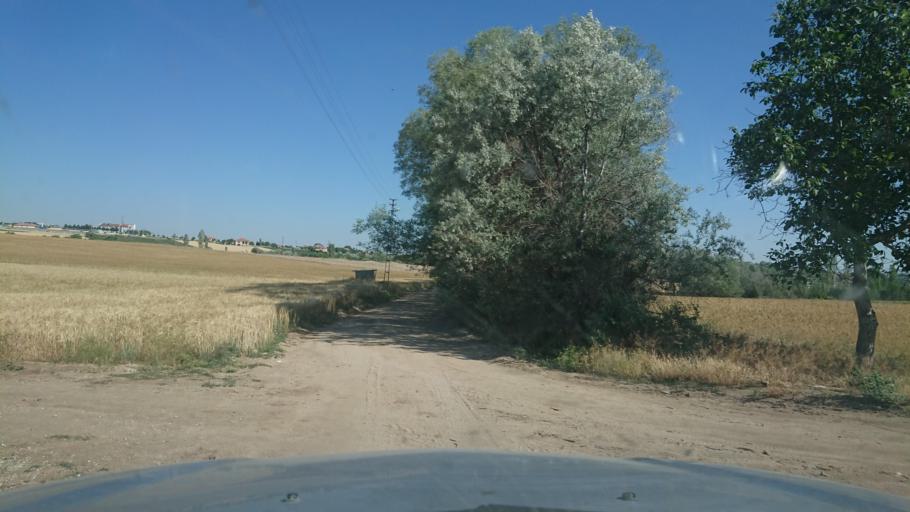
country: TR
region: Aksaray
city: Agacoren
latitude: 38.8576
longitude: 33.9126
